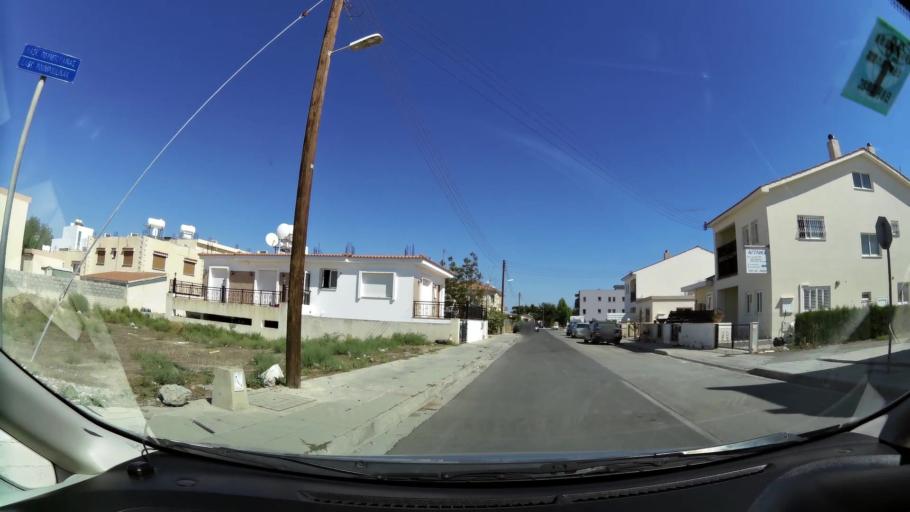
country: CY
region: Larnaka
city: Livadia
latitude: 34.9599
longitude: 33.6350
